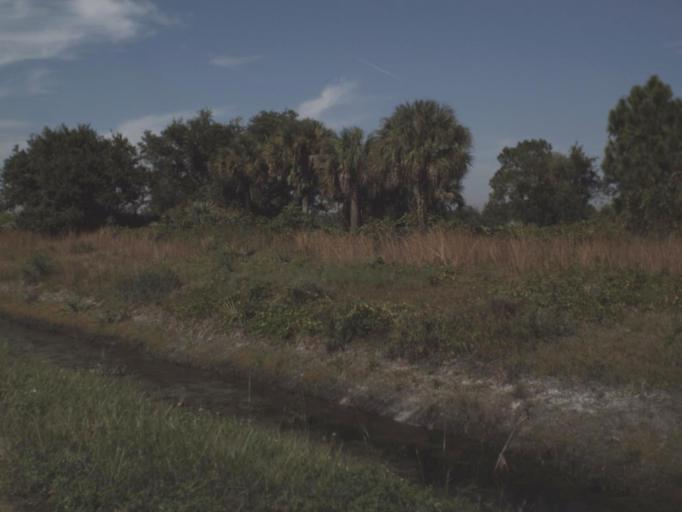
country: US
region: Florida
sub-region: Brevard County
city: Titusville
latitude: 28.6436
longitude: -80.7210
